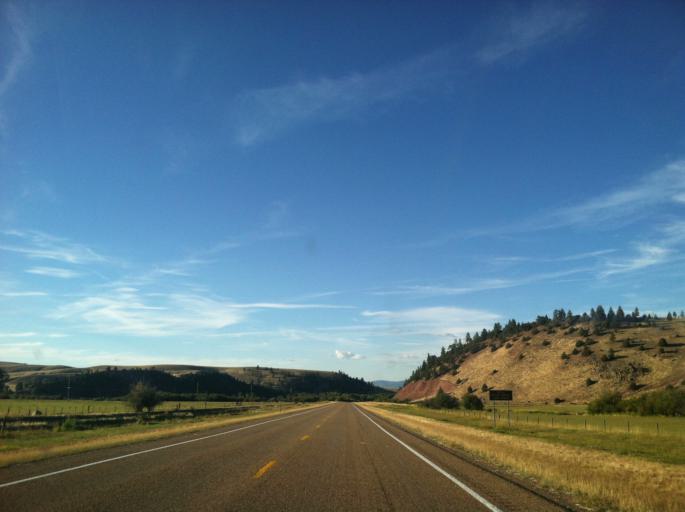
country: US
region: Montana
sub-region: Granite County
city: Philipsburg
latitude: 46.5080
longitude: -113.2257
